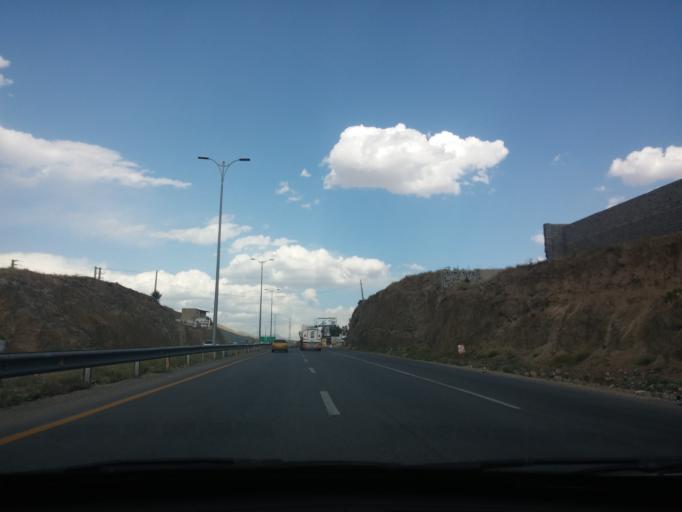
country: IR
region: Tehran
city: Damavand
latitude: 35.7197
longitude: 51.9081
